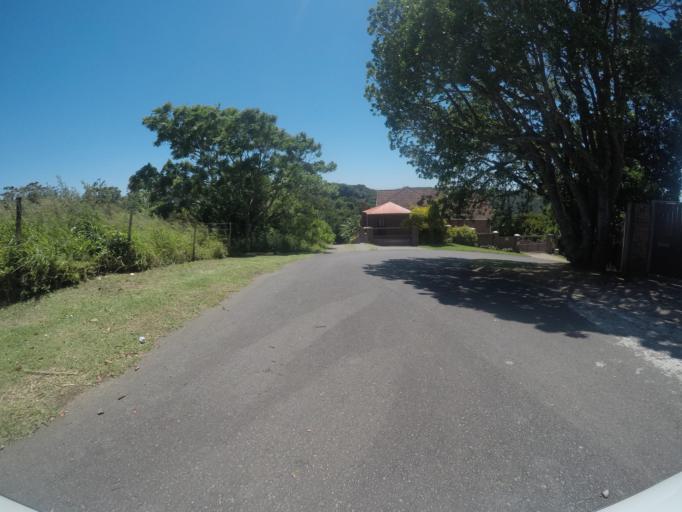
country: ZA
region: Eastern Cape
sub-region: Buffalo City Metropolitan Municipality
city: East London
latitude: -32.9361
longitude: 28.0067
